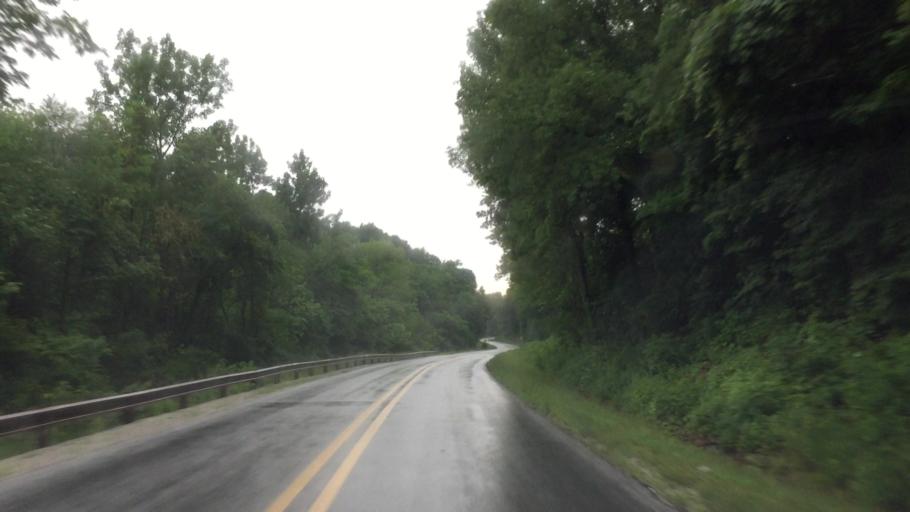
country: US
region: Iowa
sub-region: Lee County
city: Fort Madison
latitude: 40.6073
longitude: -91.2791
